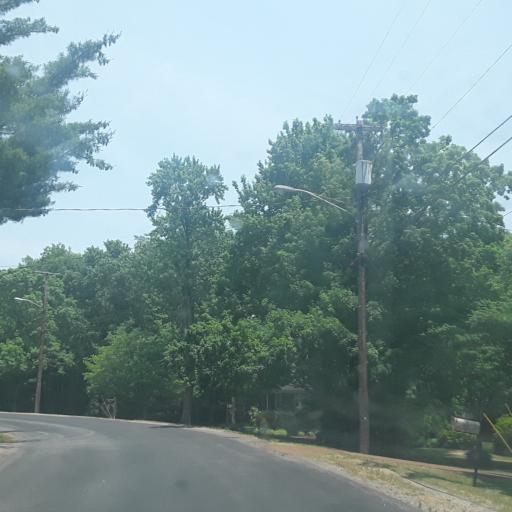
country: US
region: Tennessee
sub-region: Davidson County
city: Oak Hill
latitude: 36.0619
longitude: -86.7545
